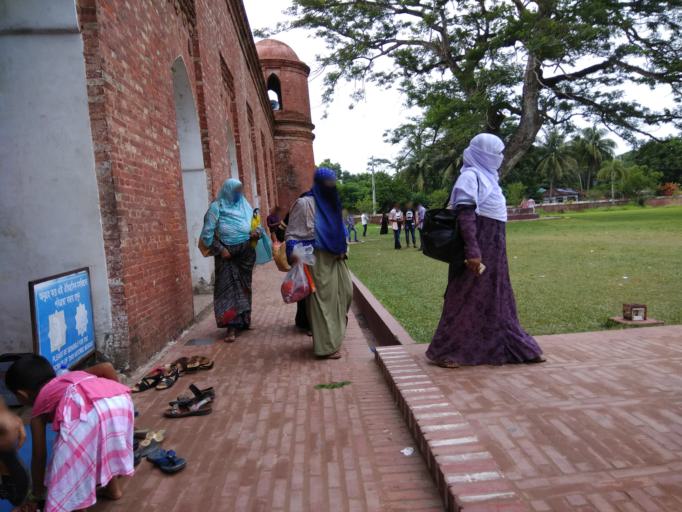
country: BD
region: Khulna
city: Khulna
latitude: 22.6744
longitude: 89.7419
